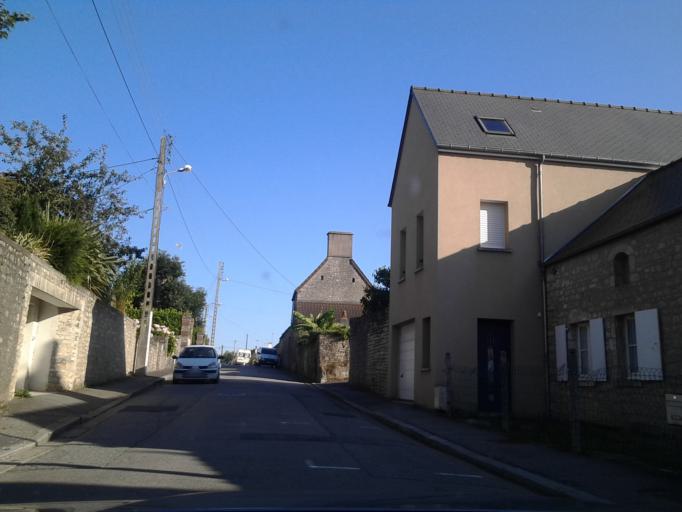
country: FR
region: Lower Normandy
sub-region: Departement de la Manche
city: Valognes
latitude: 49.5142
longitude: -1.4745
